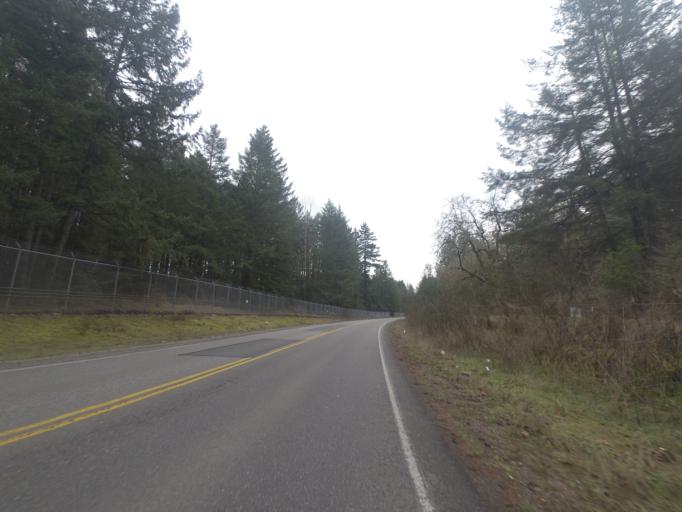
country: US
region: Washington
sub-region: Pierce County
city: McChord Air Force Base
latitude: 47.1204
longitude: -122.5075
